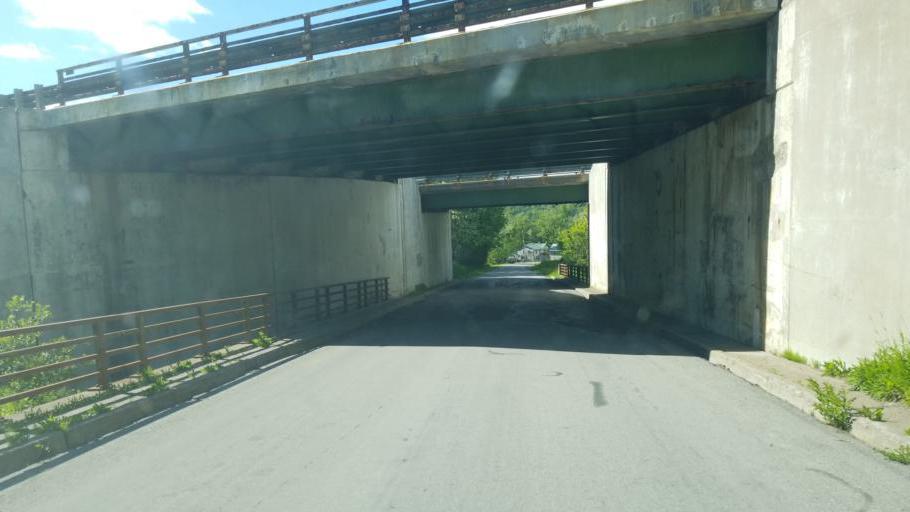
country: US
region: New York
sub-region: Montgomery County
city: Saint Johnsville
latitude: 42.9889
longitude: -74.7165
